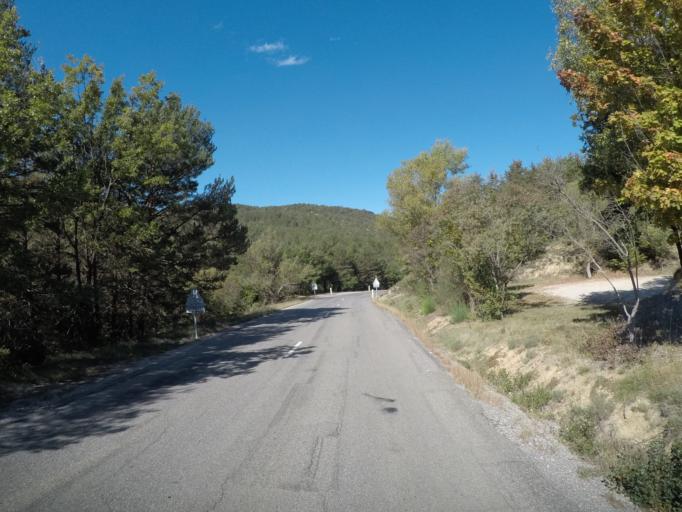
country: FR
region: Provence-Alpes-Cote d'Azur
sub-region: Departement des Alpes-de-Haute-Provence
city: Mallemoisson
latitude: 44.0250
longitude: 6.1717
